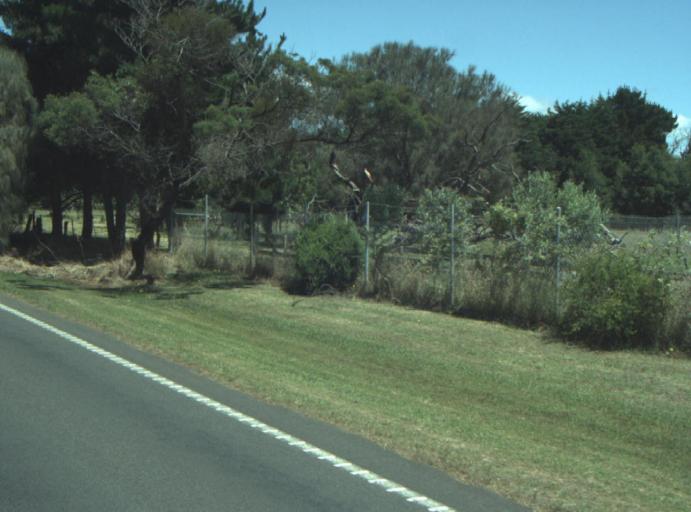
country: AU
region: Victoria
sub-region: Queenscliffe
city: Queenscliff
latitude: -38.1783
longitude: 144.6998
